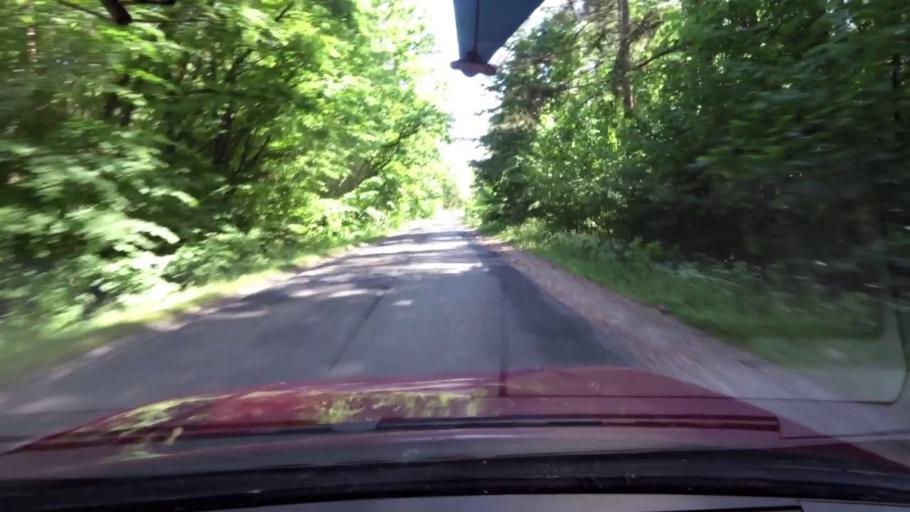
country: PL
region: Pomeranian Voivodeship
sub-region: Powiat slupski
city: Kepice
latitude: 54.3308
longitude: 16.9608
